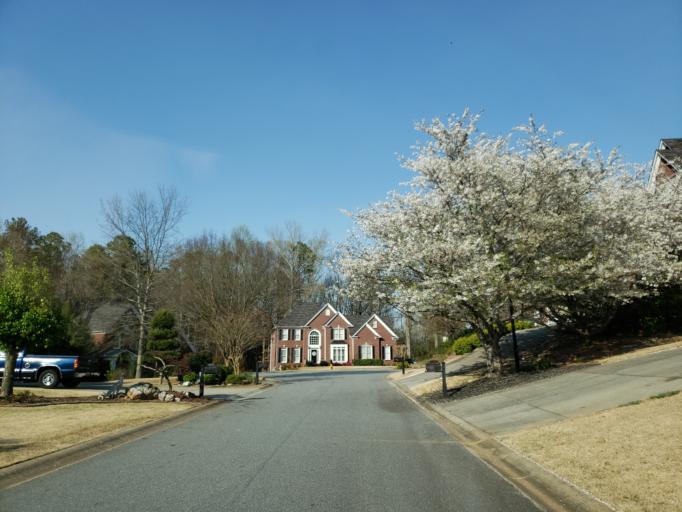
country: US
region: Georgia
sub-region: Cobb County
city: Marietta
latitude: 33.9844
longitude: -84.5050
